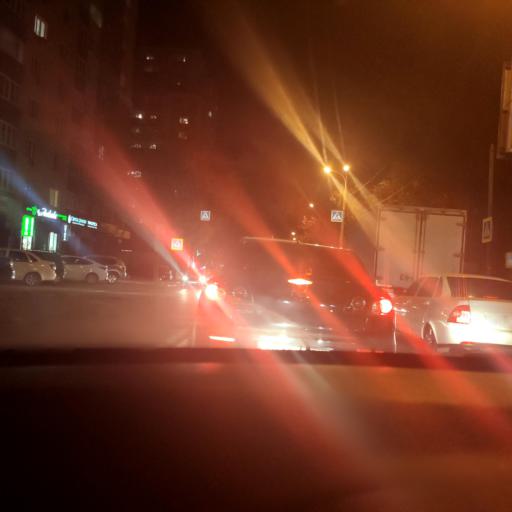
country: RU
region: Samara
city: Samara
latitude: 53.2070
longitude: 50.1768
